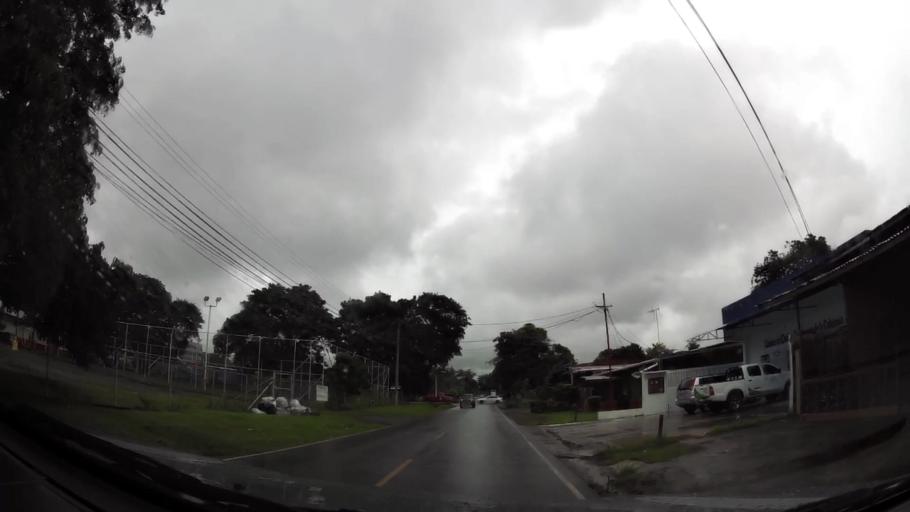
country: PA
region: Chiriqui
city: David
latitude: 8.4323
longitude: -82.4338
